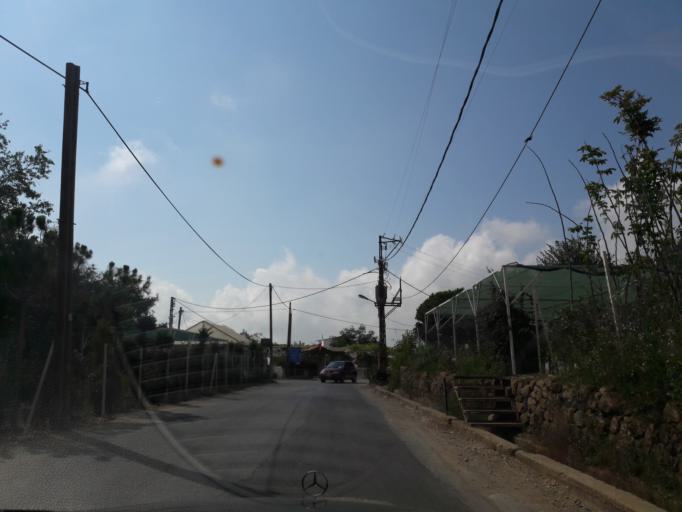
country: LB
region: Mont-Liban
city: Djounie
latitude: 33.9550
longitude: 35.7762
